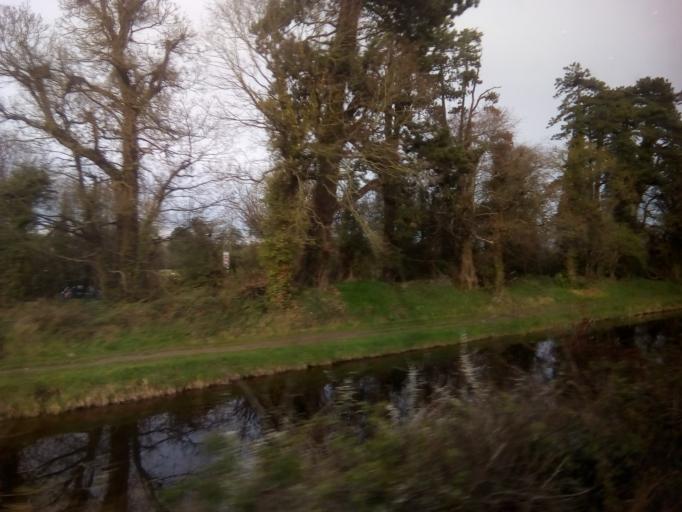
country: IE
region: Leinster
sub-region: Kildare
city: Celbridge
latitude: 53.3753
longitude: -6.5374
